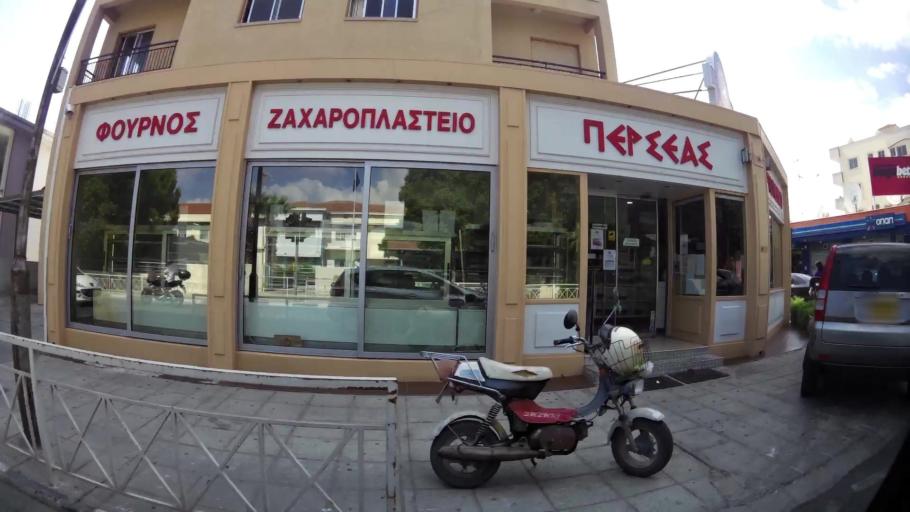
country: CY
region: Larnaka
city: Larnaca
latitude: 34.9175
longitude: 33.6219
